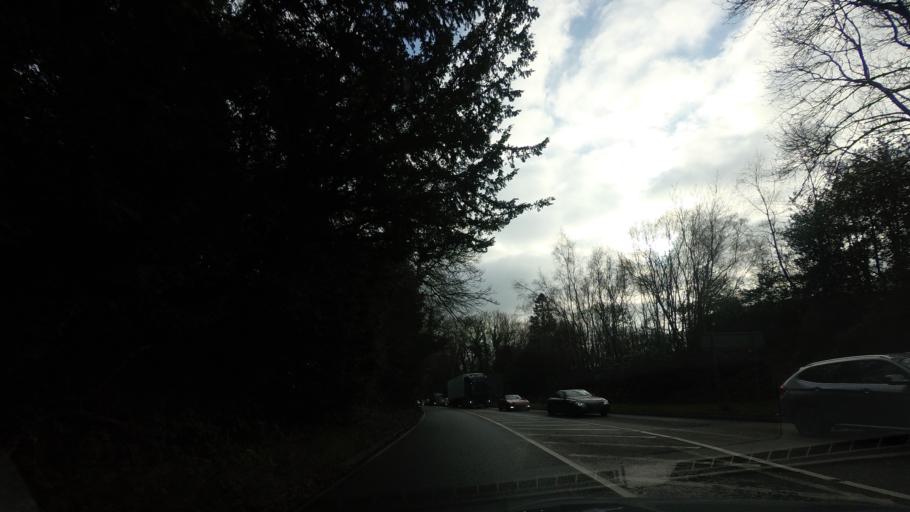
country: GB
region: England
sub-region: Kent
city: Hawkhurst
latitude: 51.0539
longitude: 0.4462
